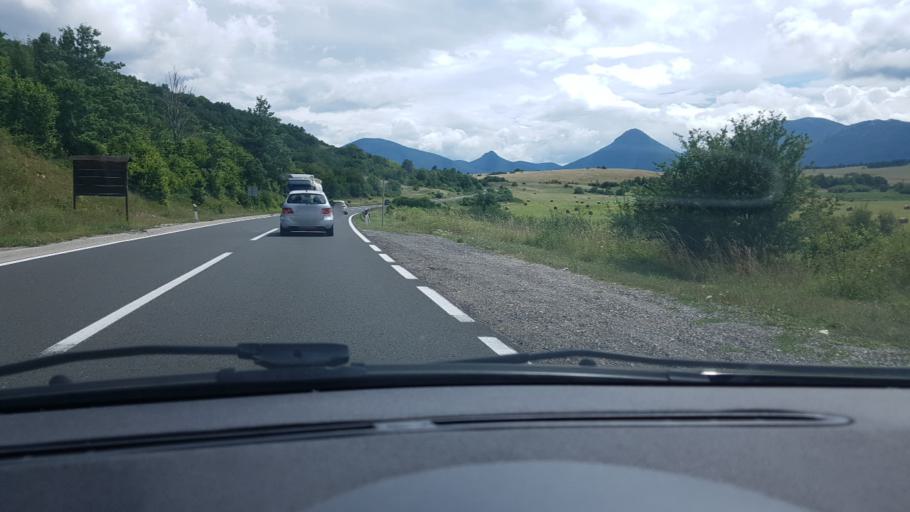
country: HR
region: Zadarska
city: Gracac
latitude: 44.4967
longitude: 15.7639
